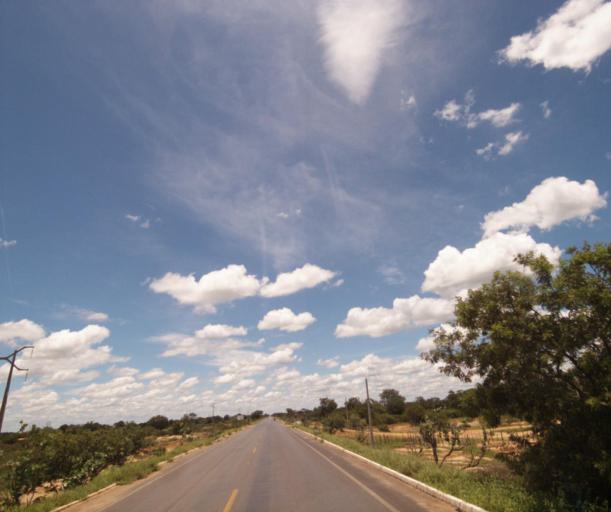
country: BR
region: Bahia
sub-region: Bom Jesus Da Lapa
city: Bom Jesus da Lapa
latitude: -13.2568
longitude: -43.4545
